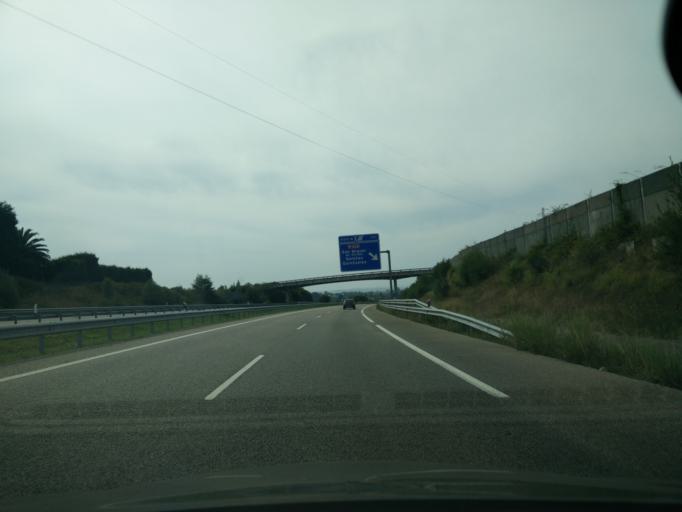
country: ES
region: Asturias
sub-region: Province of Asturias
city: Arriba
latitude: 43.5088
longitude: -5.5584
